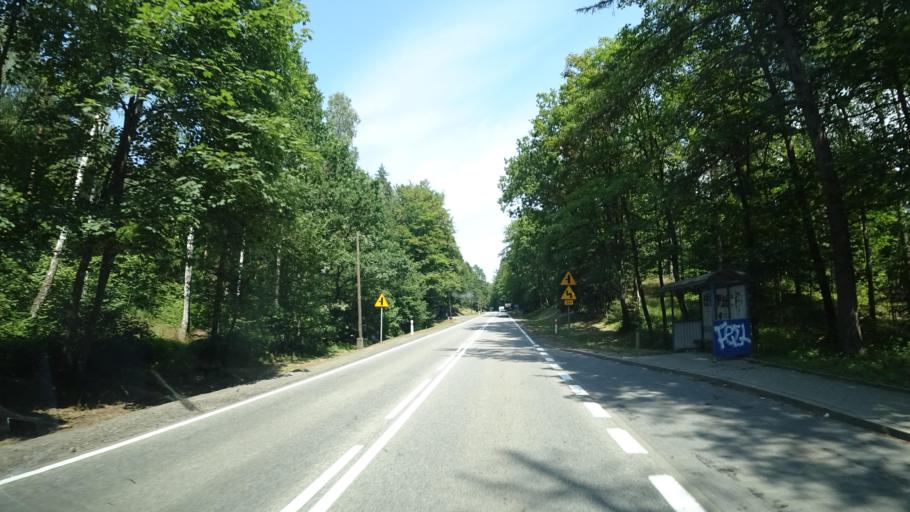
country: PL
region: Pomeranian Voivodeship
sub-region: Powiat koscierski
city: Grabowo Koscierskie
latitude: 54.2149
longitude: 18.1181
